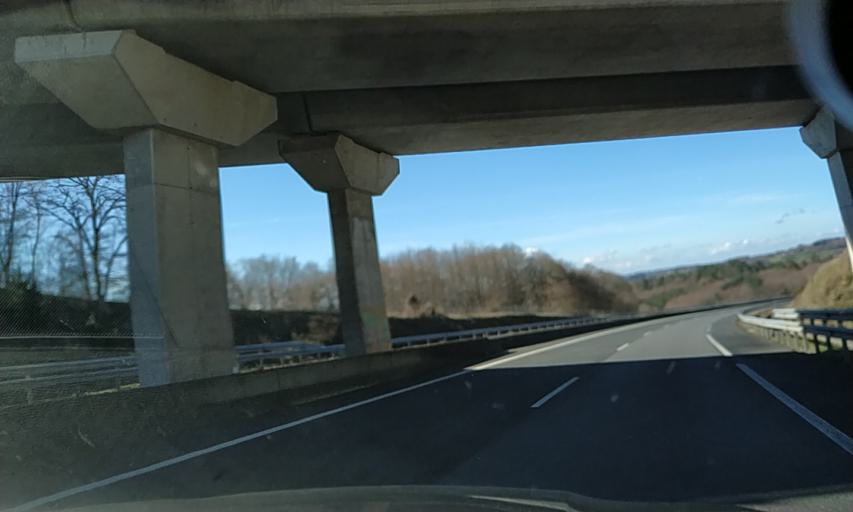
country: ES
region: Galicia
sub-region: Provincia de Pontevedra
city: Lalin
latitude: 42.6258
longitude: -8.1149
